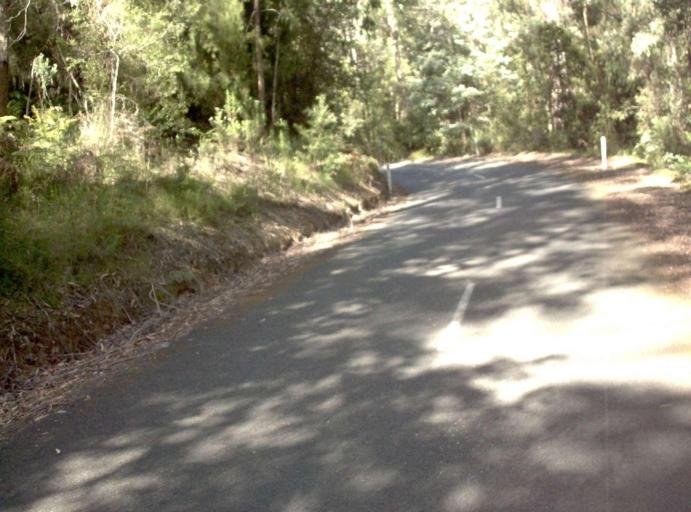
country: AU
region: Victoria
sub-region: East Gippsland
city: Lakes Entrance
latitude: -37.4441
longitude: 148.5851
